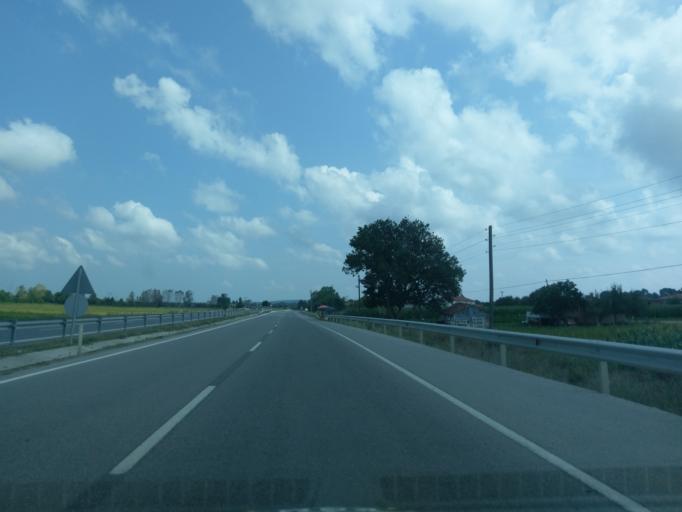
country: TR
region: Samsun
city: Bafra
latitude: 41.5990
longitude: 35.7736
